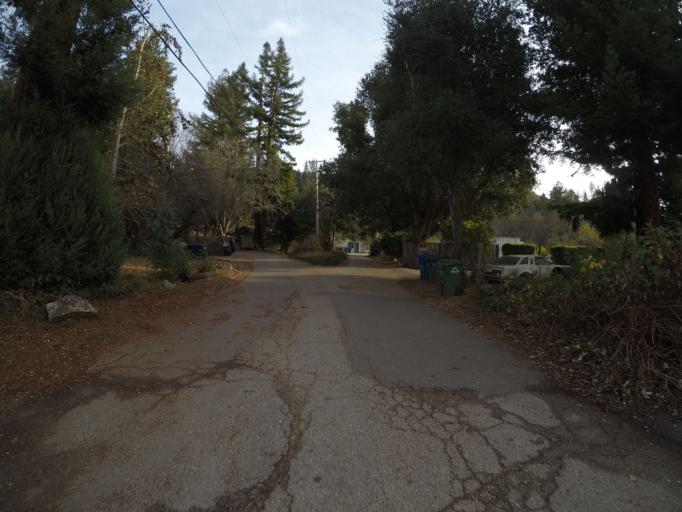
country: US
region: California
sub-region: Santa Cruz County
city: Scotts Valley
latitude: 37.0570
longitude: -122.0280
